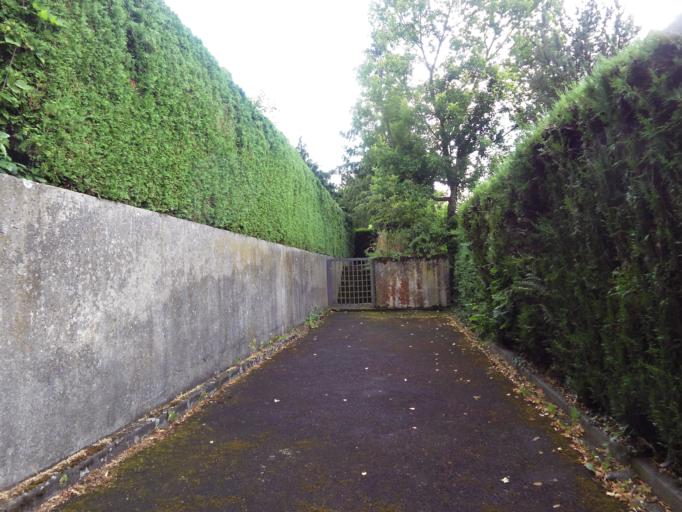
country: DE
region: Bavaria
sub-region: Regierungsbezirk Unterfranken
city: Wuerzburg
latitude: 49.8079
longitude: 9.9650
